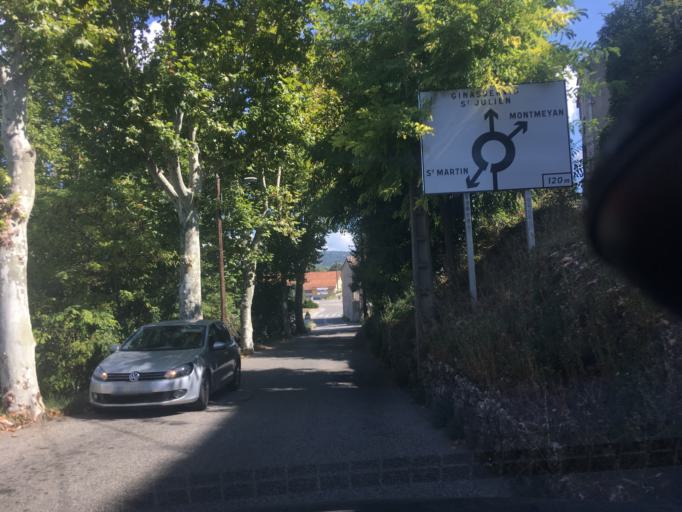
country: FR
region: Provence-Alpes-Cote d'Azur
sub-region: Departement du Var
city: Saint-Julien
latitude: 43.6391
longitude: 5.9342
